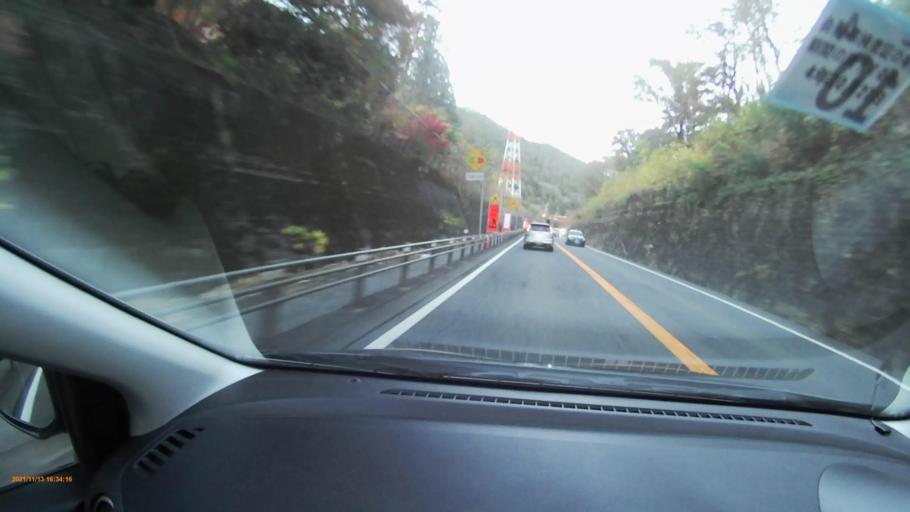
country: JP
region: Gifu
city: Nakatsugawa
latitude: 35.5916
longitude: 137.5982
